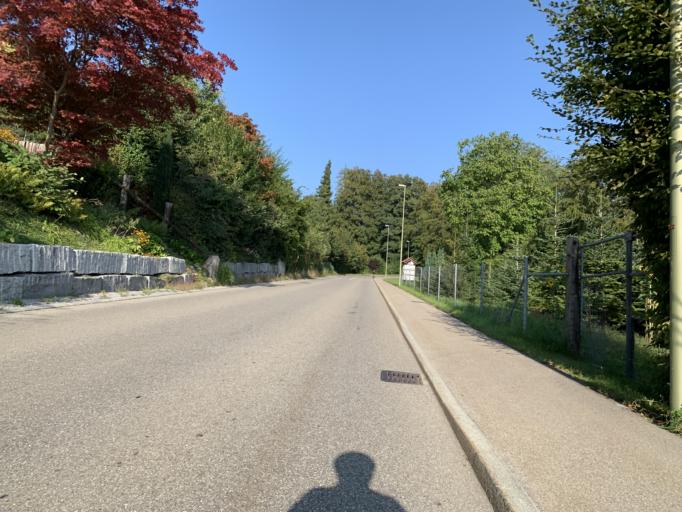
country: CH
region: Zurich
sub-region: Bezirk Hinwil
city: Hinwil
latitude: 47.3070
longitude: 8.8501
